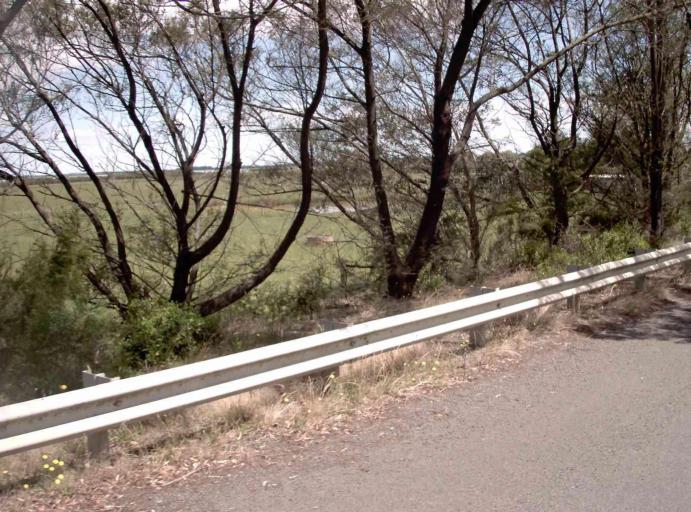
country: AU
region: Victoria
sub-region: Cardinia
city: Koo-Wee-Rup
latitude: -38.3507
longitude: 145.5585
